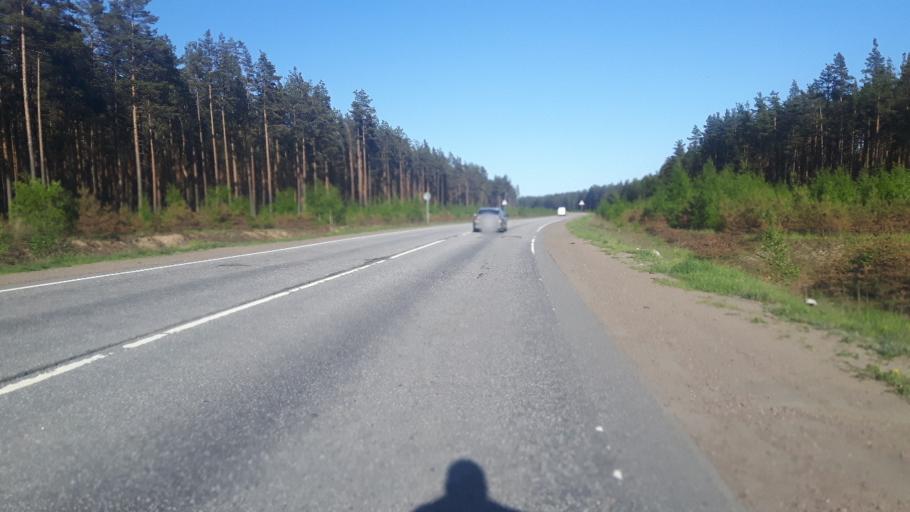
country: RU
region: Leningrad
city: Lebyazh'ye
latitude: 60.1680
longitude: 29.2404
